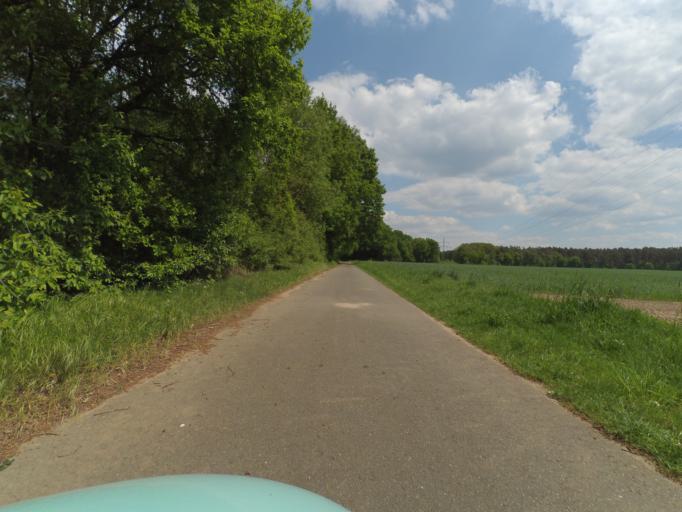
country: DE
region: Lower Saxony
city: Wietze
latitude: 52.6795
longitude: 9.8573
